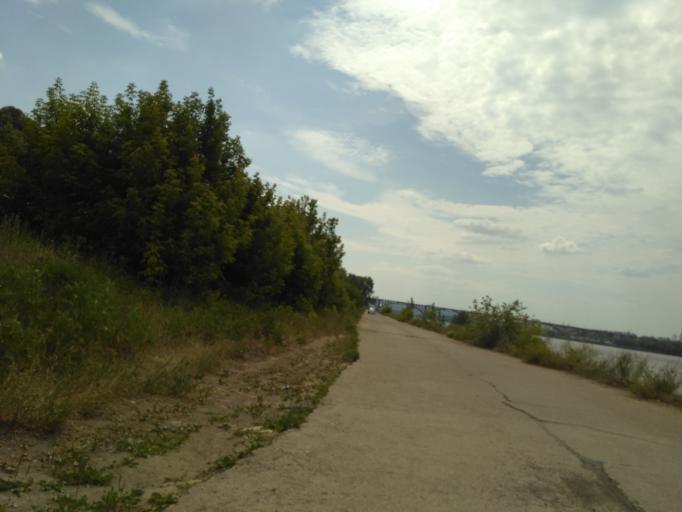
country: RU
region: Nizjnij Novgorod
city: Nizhniy Novgorod
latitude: 56.3138
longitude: 43.9687
